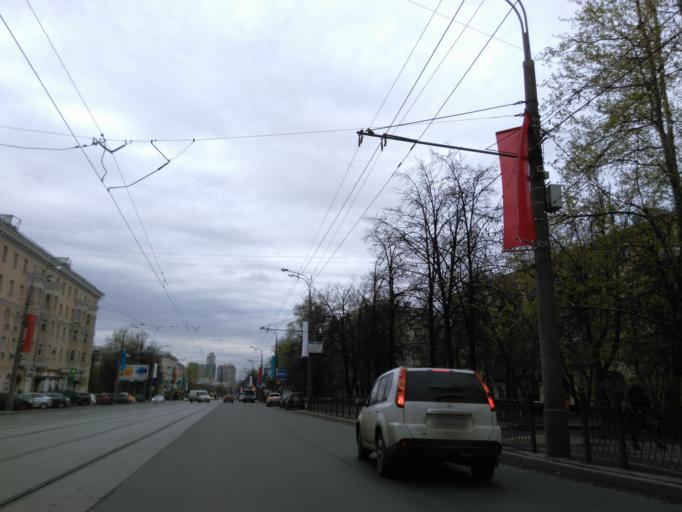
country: RU
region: Moscow
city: Pokrovskoye-Streshnevo
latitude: 55.8341
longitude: 37.4538
